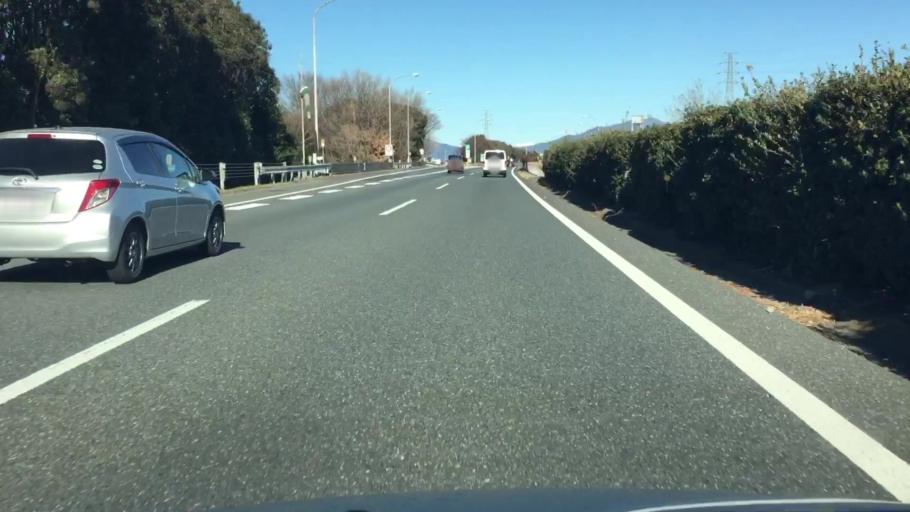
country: JP
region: Gunma
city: Kanekomachi
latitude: 36.4274
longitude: 139.0159
